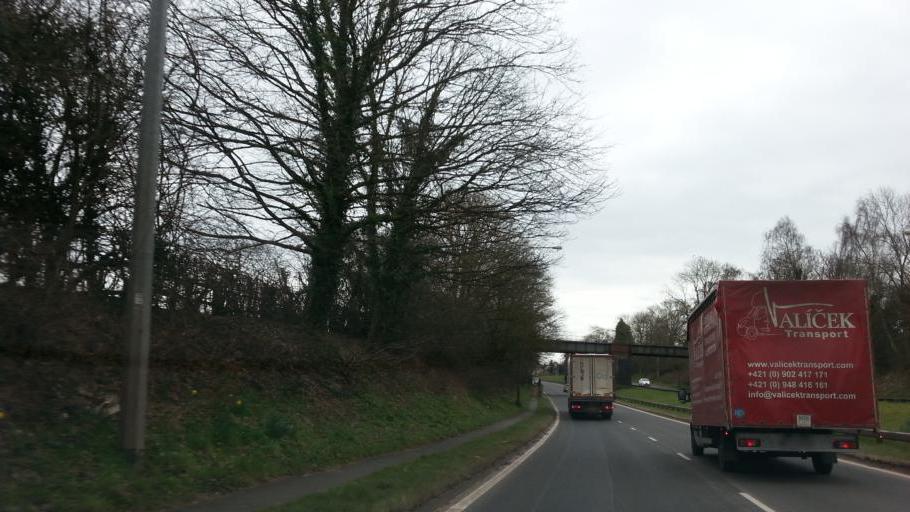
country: GB
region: England
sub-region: Staffordshire
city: Stone
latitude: 52.9026
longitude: -2.1597
